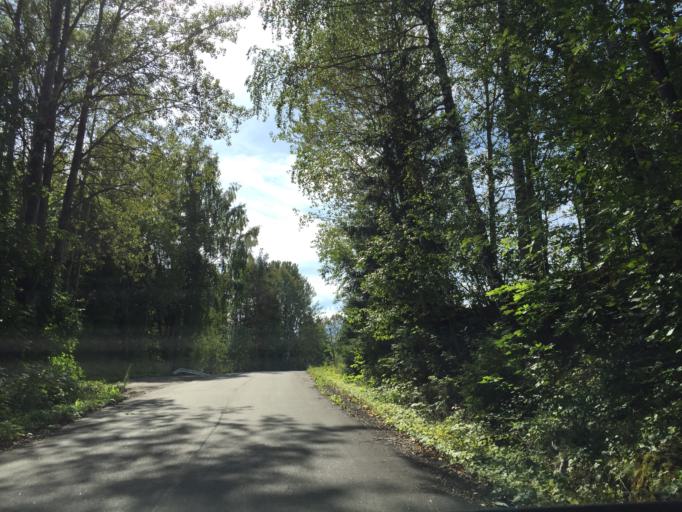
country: NO
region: Vestfold
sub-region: Hof
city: Hof
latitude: 59.4652
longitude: 10.1468
